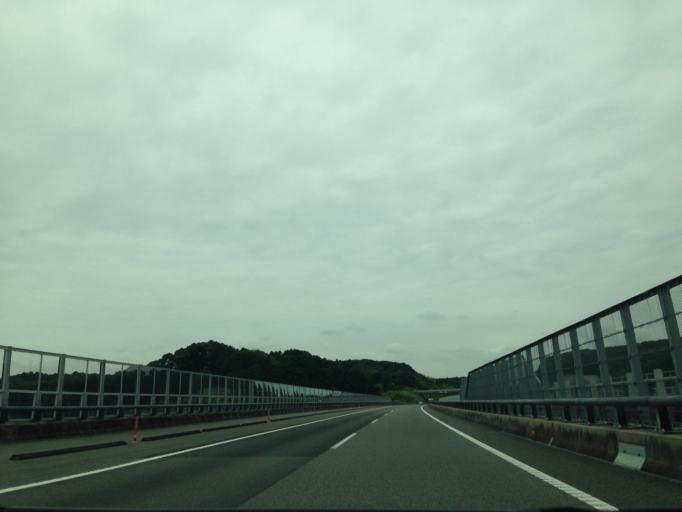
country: JP
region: Shizuoka
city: Mori
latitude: 34.8252
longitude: 137.8650
